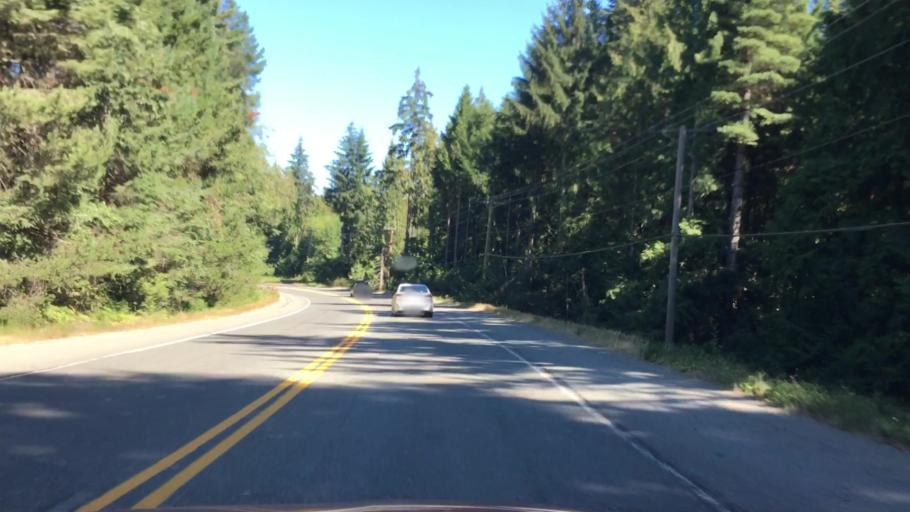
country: CA
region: British Columbia
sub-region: Regional District of Nanaimo
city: Parksville
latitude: 49.3109
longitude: -124.5264
